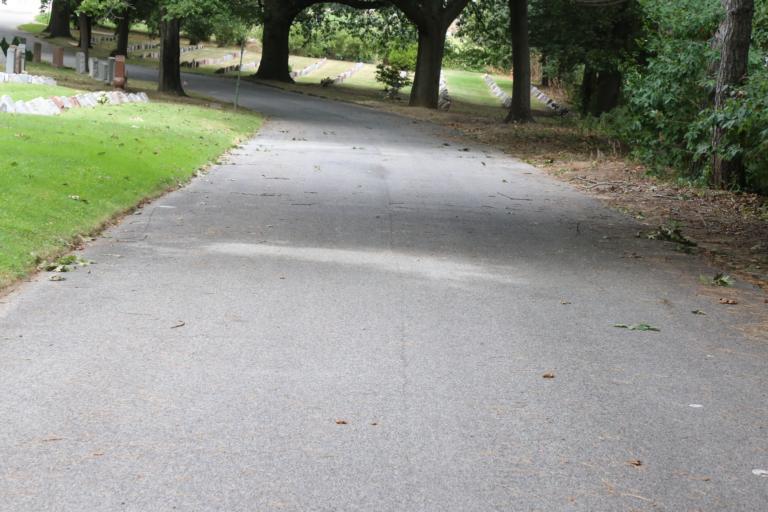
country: US
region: New York
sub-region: Bronx
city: The Bronx
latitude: 40.8807
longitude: -73.8710
